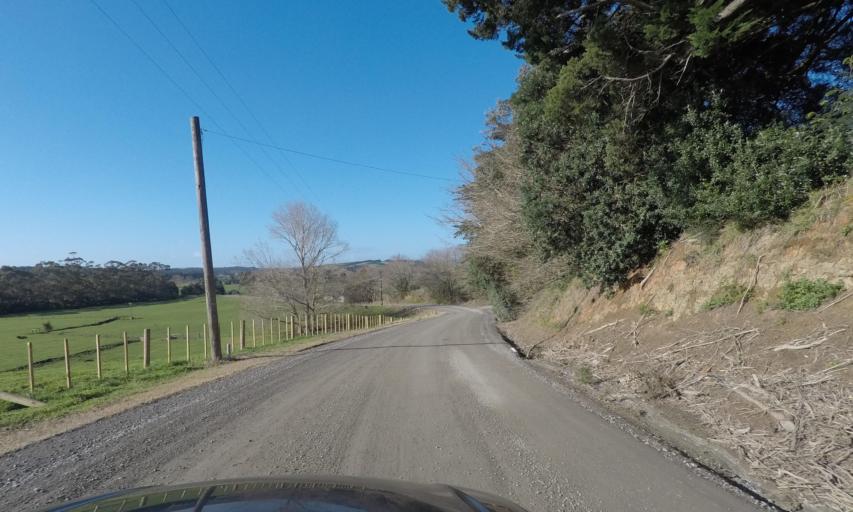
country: NZ
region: Auckland
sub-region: Auckland
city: Wellsford
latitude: -36.1451
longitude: 174.5989
